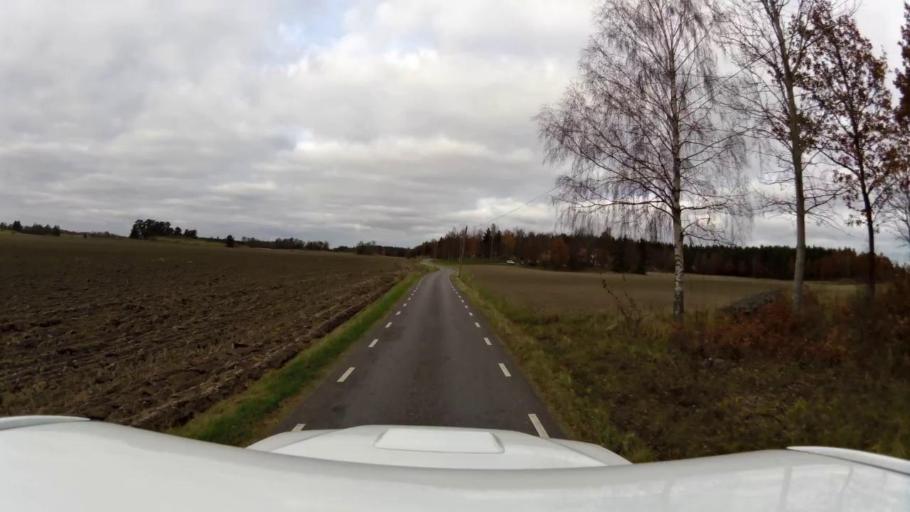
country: SE
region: OEstergoetland
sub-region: Linkopings Kommun
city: Linghem
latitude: 58.3851
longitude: 15.8168
